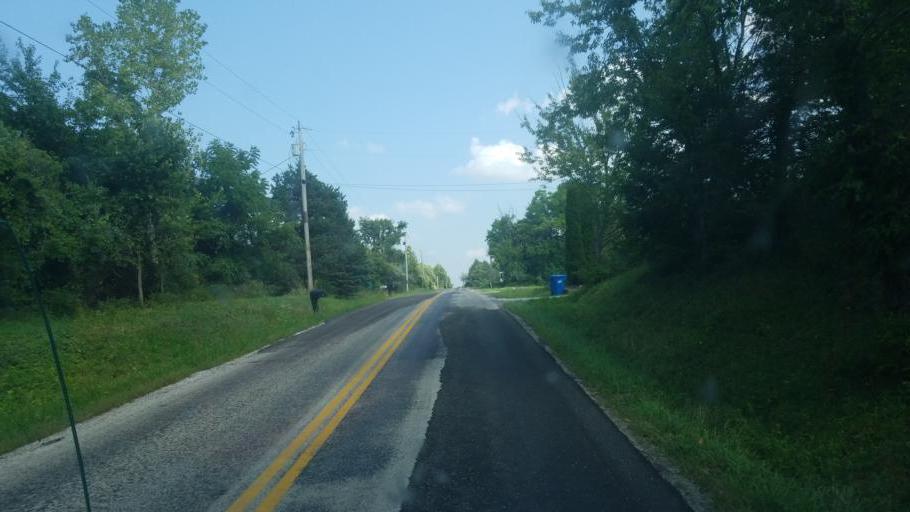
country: US
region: Ohio
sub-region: Huron County
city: New London
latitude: 41.0658
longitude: -82.3320
